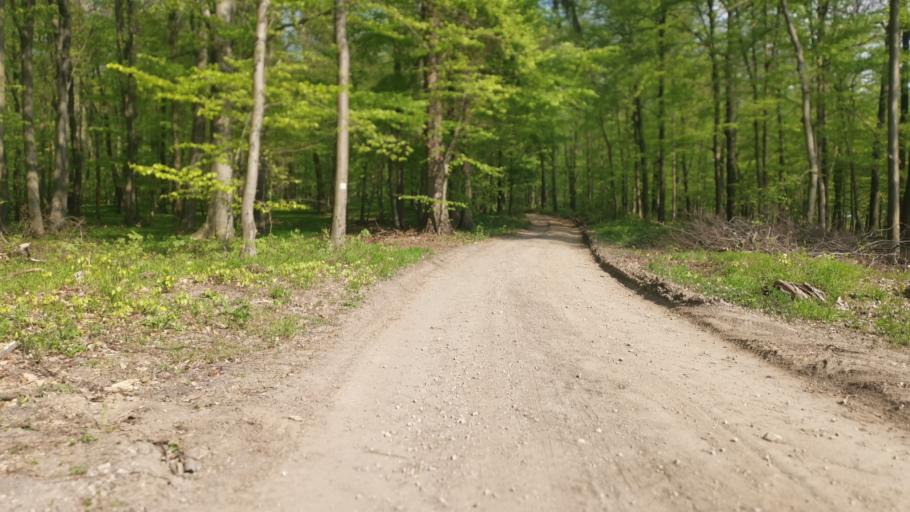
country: SK
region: Trnavsky
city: Smolenice
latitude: 48.5713
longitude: 17.3720
